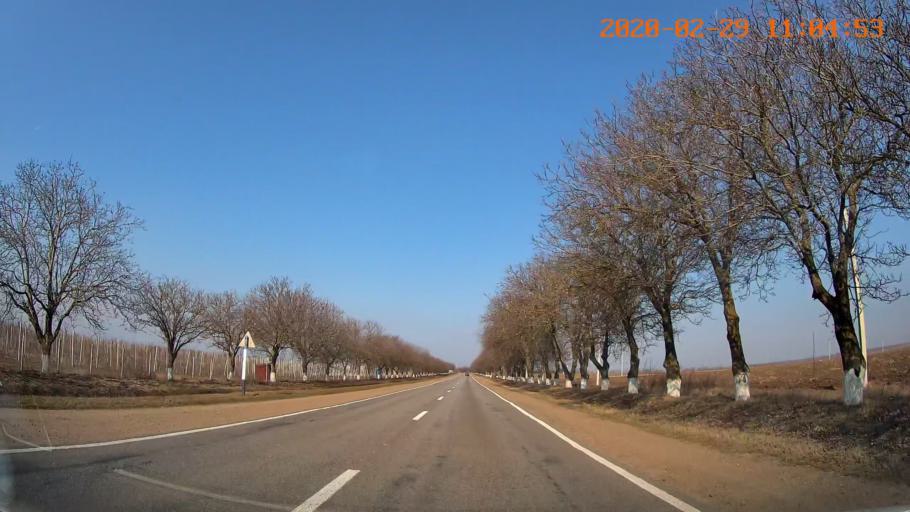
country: MD
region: Criuleni
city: Criuleni
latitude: 47.1949
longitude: 29.1970
